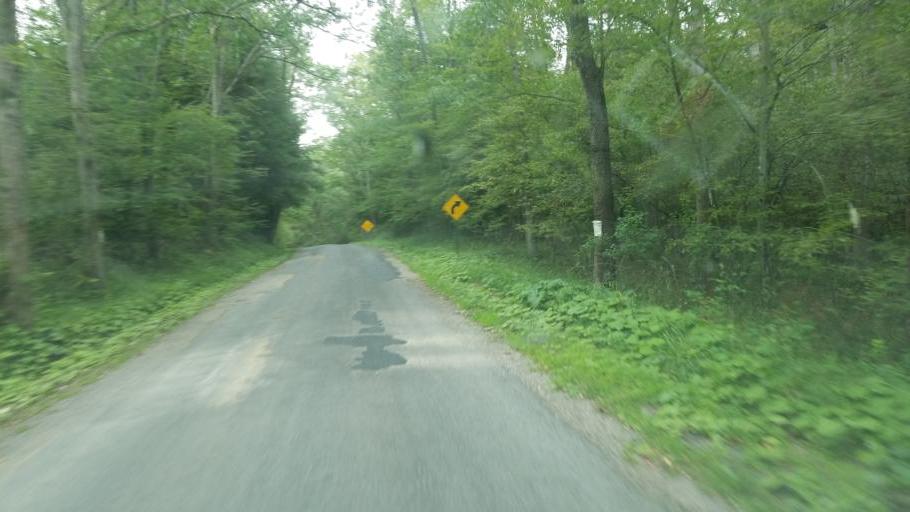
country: US
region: Pennsylvania
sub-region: Clarion County
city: Marianne
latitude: 41.2221
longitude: -79.4156
